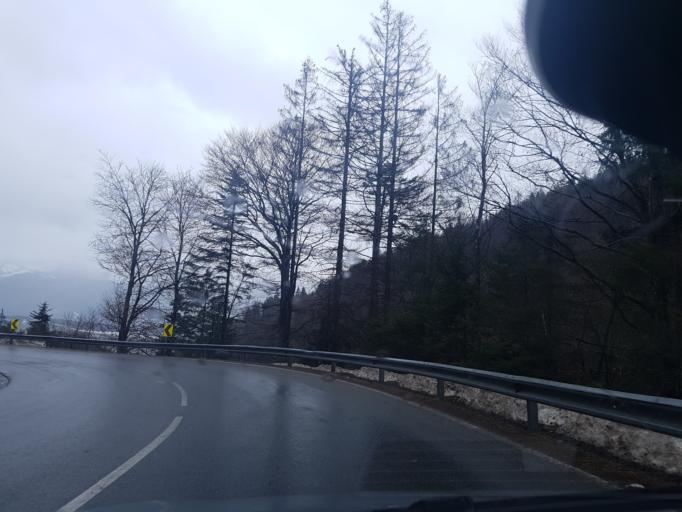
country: AT
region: Tyrol
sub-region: Politischer Bezirk Kufstein
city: Worgl
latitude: 47.4722
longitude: 12.0767
